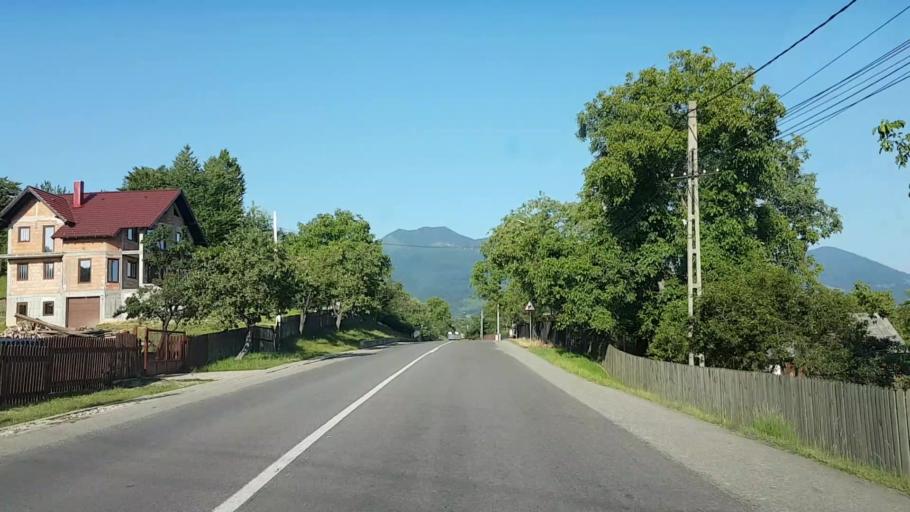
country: RO
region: Bistrita-Nasaud
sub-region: Comuna Tiha Bargaului
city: Tiha Bargaului
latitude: 47.2299
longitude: 24.7843
